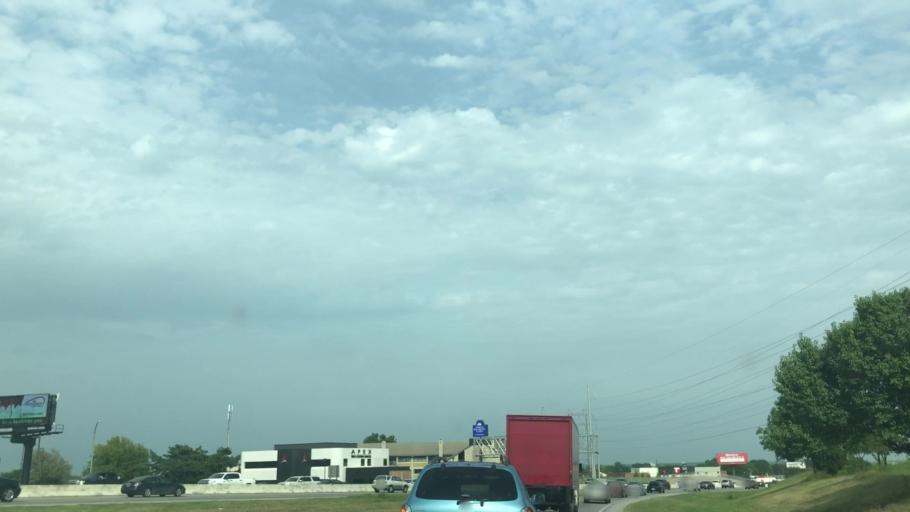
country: US
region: Oklahoma
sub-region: Tulsa County
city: Tulsa
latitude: 36.1126
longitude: -95.8943
